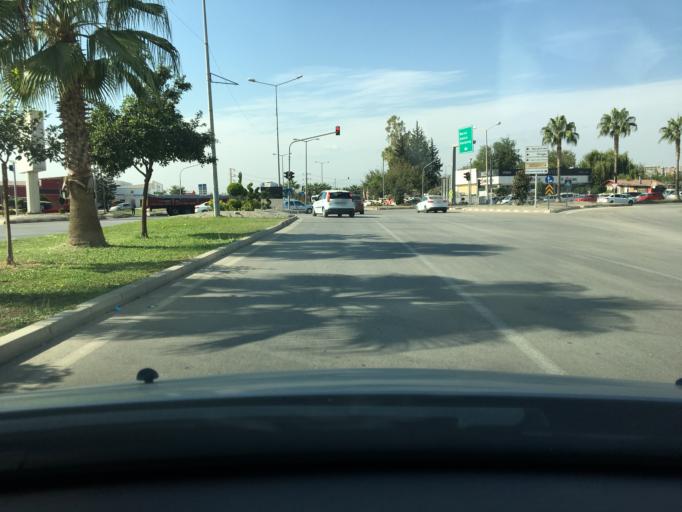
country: TR
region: Adana
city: Seyhan
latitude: 37.0234
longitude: 35.2546
